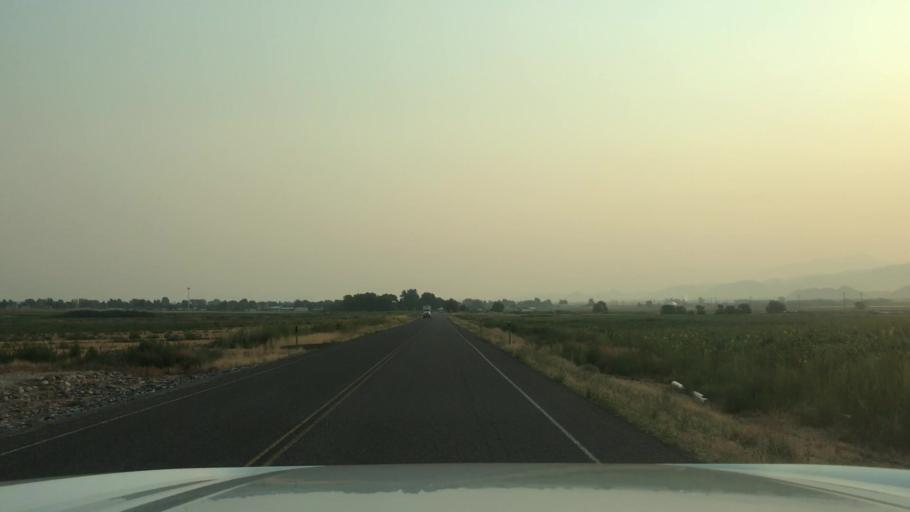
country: US
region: Utah
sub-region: Sevier County
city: Aurora
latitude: 38.9045
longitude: -111.9451
